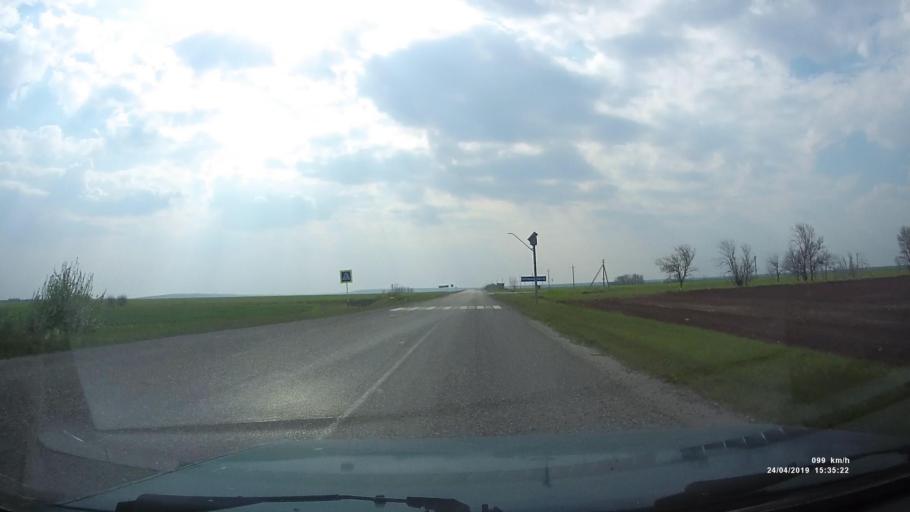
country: RU
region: Kalmykiya
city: Yashalta
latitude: 46.5994
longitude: 42.8951
